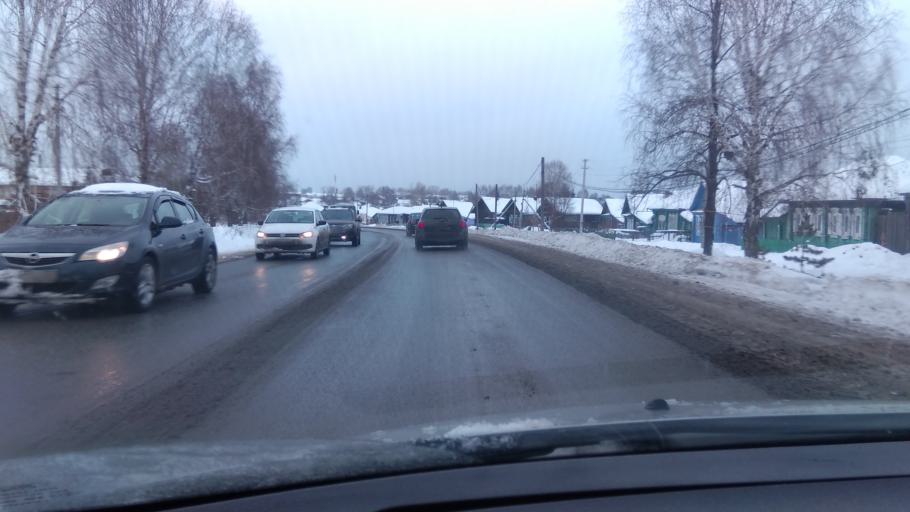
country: RU
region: Sverdlovsk
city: Nikolo-Pavlovskoye
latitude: 57.7824
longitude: 60.0599
